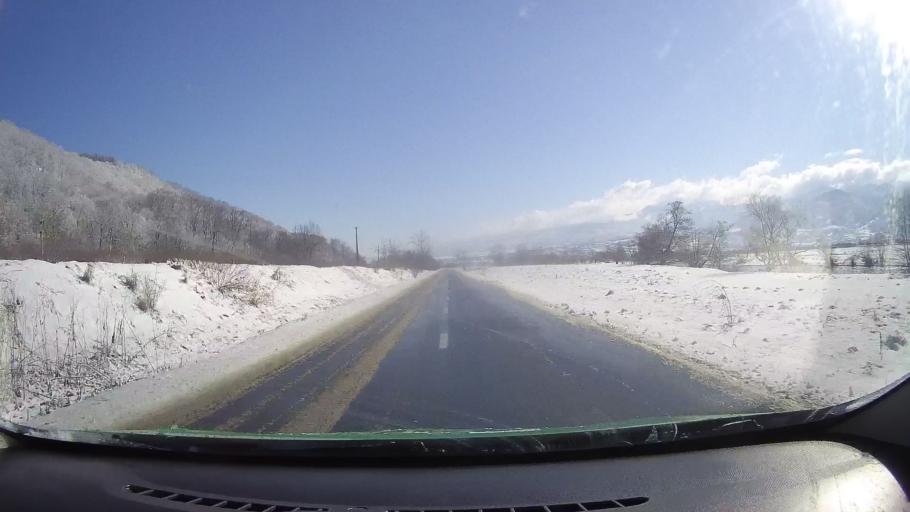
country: RO
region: Sibiu
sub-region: Comuna Talmaciu
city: Talmaciu
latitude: 45.6617
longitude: 24.2867
